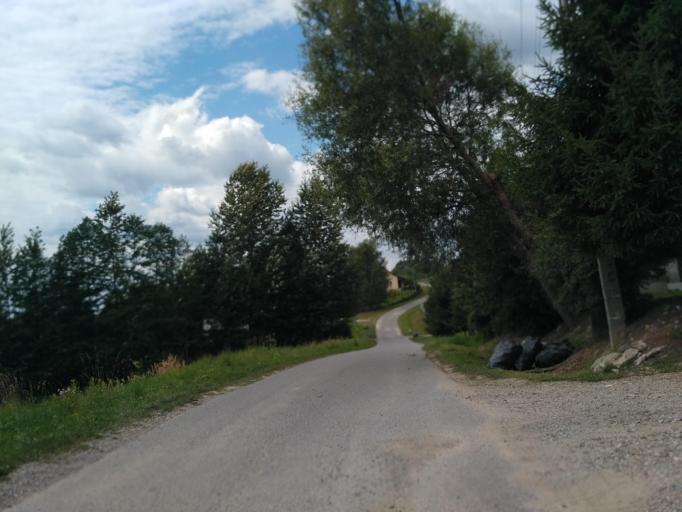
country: PL
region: Subcarpathian Voivodeship
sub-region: Powiat rzeszowski
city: Chmielnik
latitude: 49.9532
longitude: 22.1237
